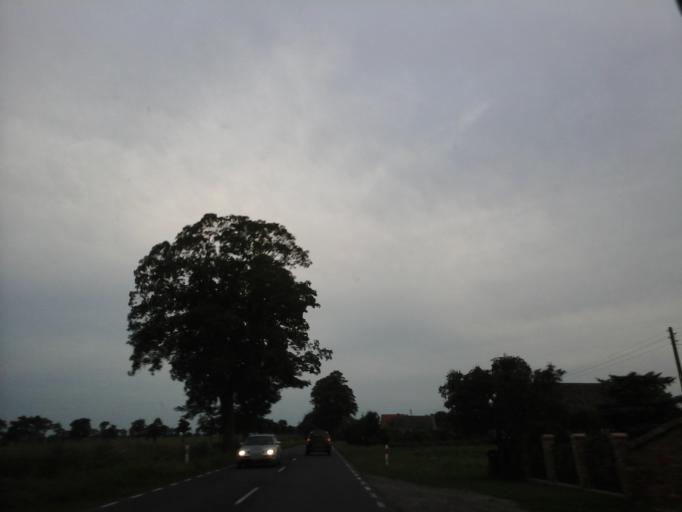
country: PL
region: West Pomeranian Voivodeship
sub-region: Powiat stargardzki
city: Stargard Szczecinski
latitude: 53.3691
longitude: 15.0720
